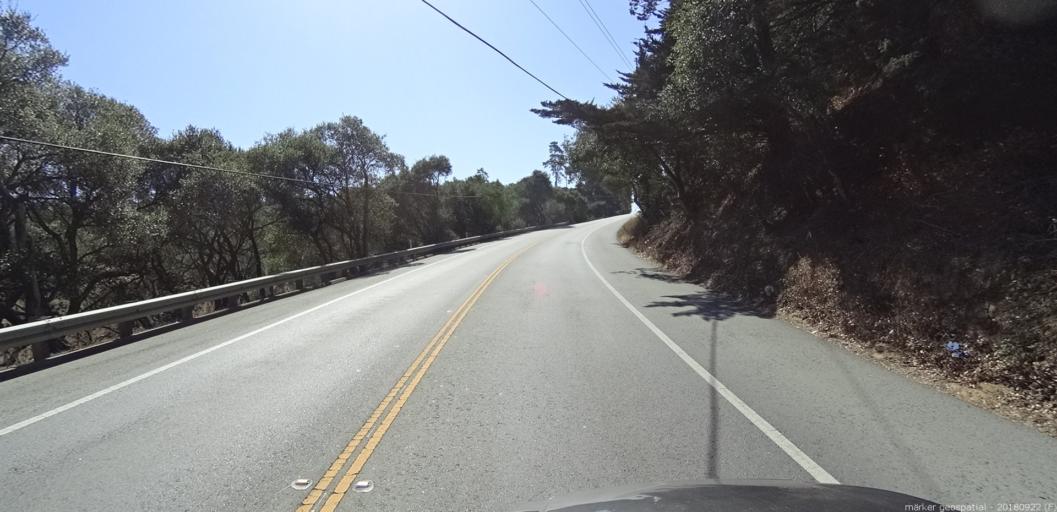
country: US
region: California
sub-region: Monterey County
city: Prunedale
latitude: 36.8338
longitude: -121.6800
